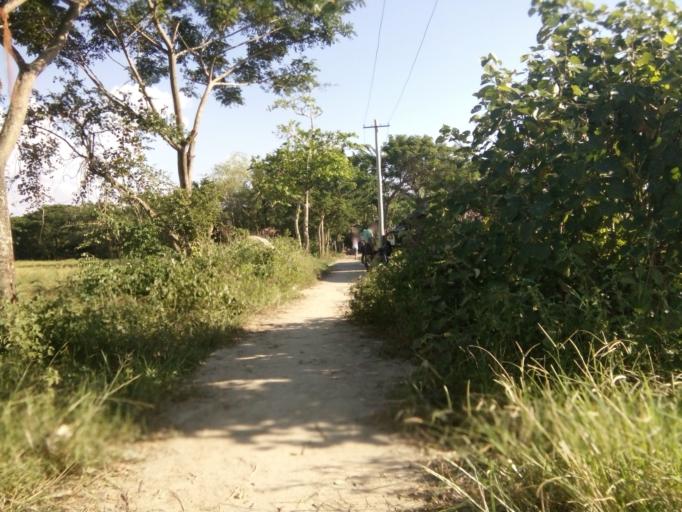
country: MM
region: Yangon
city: Kanbe
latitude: 16.8754
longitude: 95.9774
